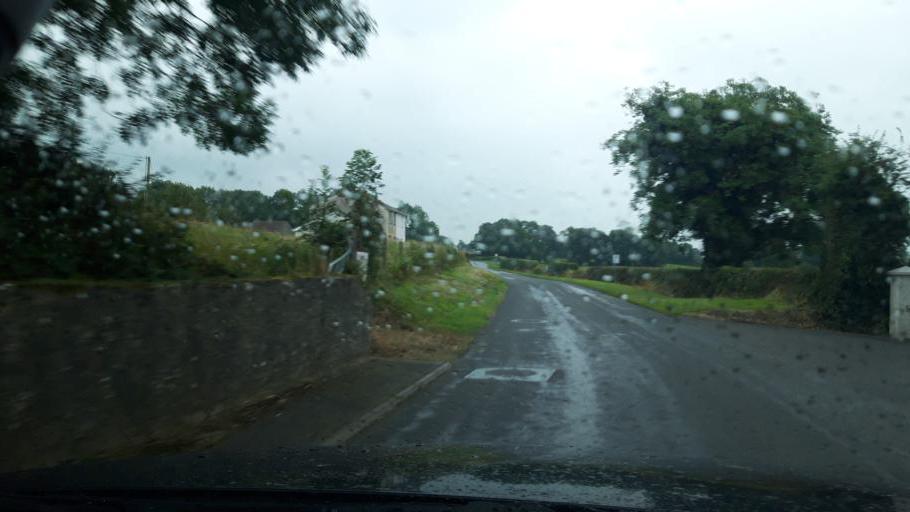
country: IE
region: Leinster
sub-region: Kilkenny
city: Callan
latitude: 52.6609
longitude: -7.4372
